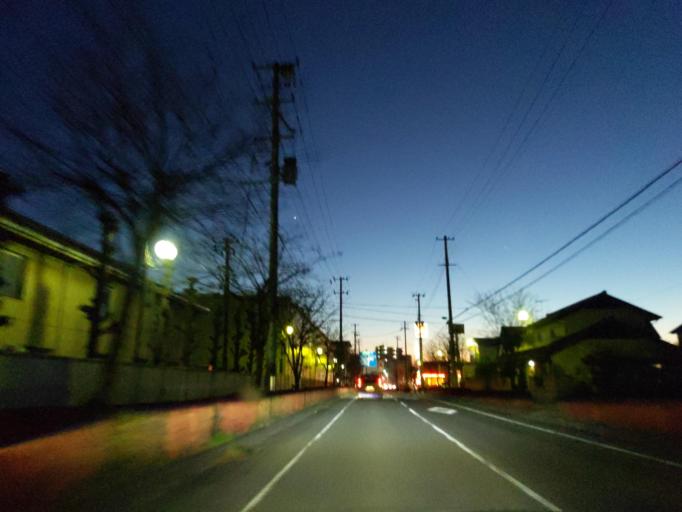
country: JP
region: Fukushima
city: Sukagawa
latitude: 37.3013
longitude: 140.3742
